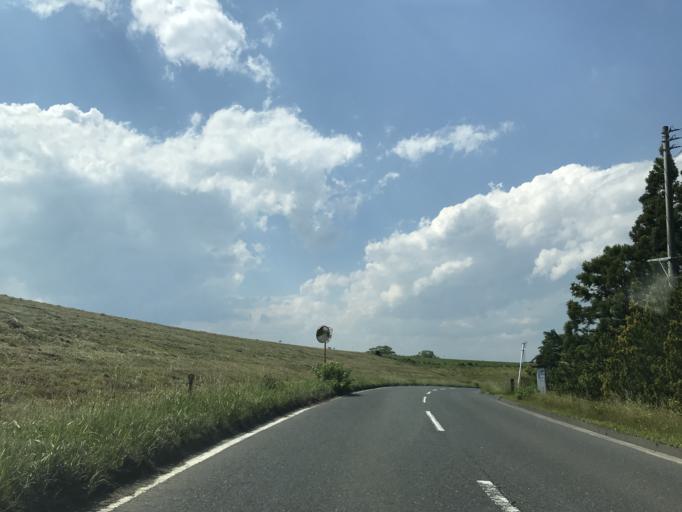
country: JP
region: Miyagi
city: Matsushima
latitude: 38.4454
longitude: 141.1116
